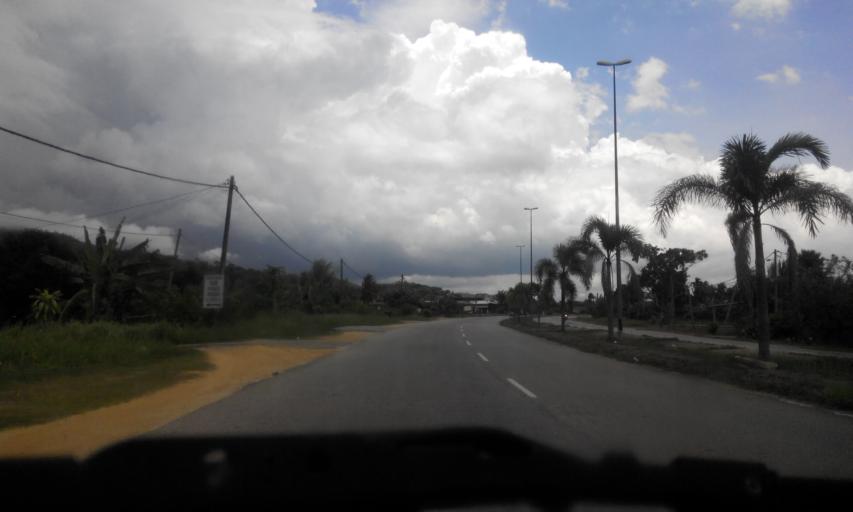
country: MY
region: Perak
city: Parit Buntar
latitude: 5.1279
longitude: 100.5104
